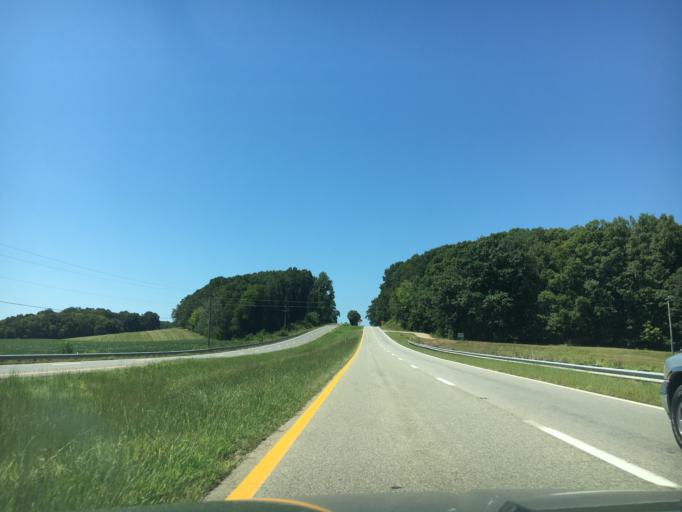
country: US
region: Virginia
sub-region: City of Danville
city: Danville
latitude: 36.5821
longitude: -79.1654
